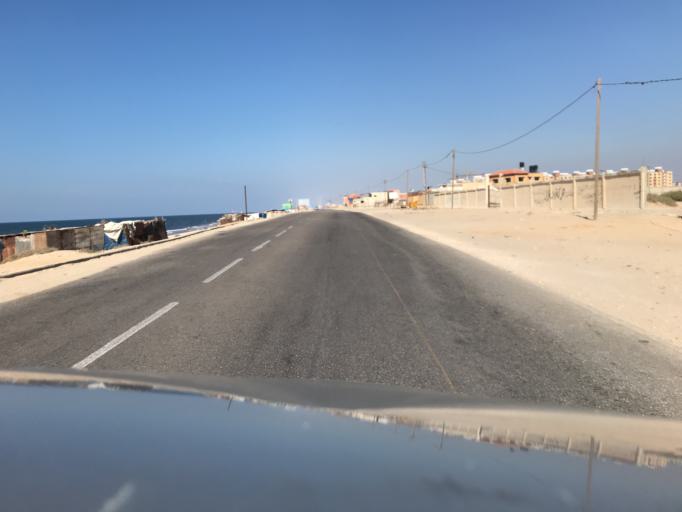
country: PS
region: Gaza Strip
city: An Nusayrat
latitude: 31.4666
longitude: 34.3789
